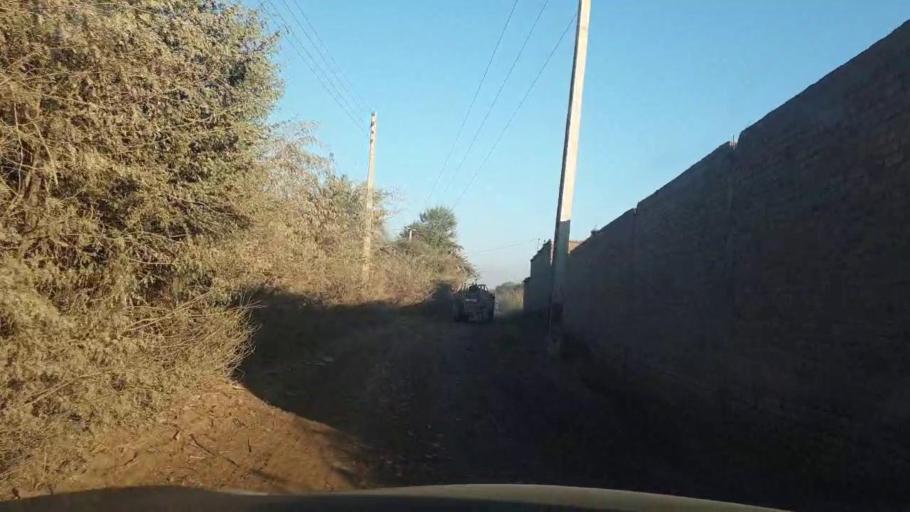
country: PK
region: Sindh
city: Ghotki
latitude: 28.0974
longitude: 69.3686
